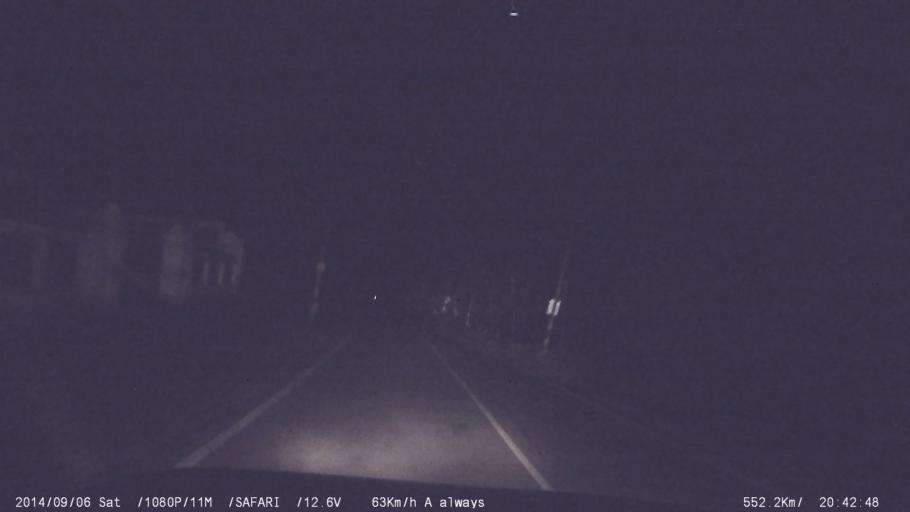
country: IN
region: Kerala
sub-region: Kottayam
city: Palackattumala
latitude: 9.6996
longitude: 76.5562
